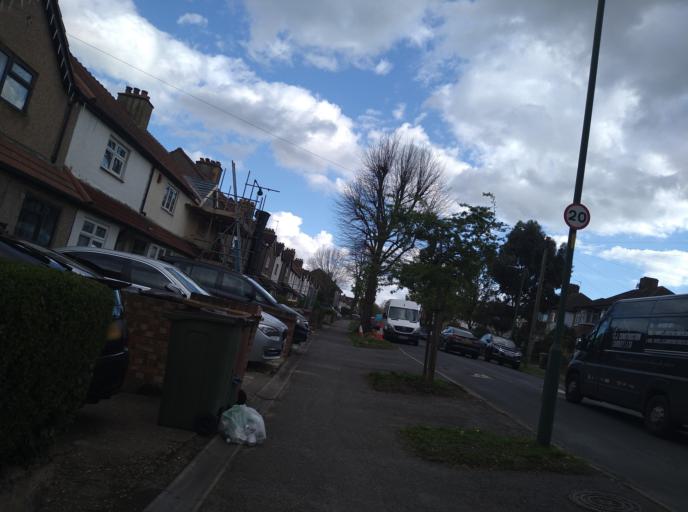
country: GB
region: England
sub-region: Greater London
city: Carshalton
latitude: 51.3708
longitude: -0.1834
